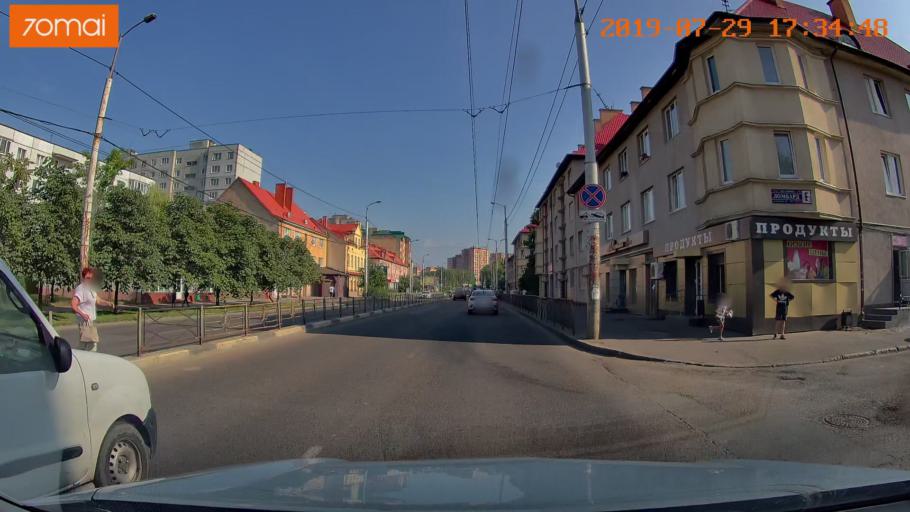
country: RU
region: Kaliningrad
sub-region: Gorod Kaliningrad
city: Kaliningrad
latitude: 54.7378
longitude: 20.5066
